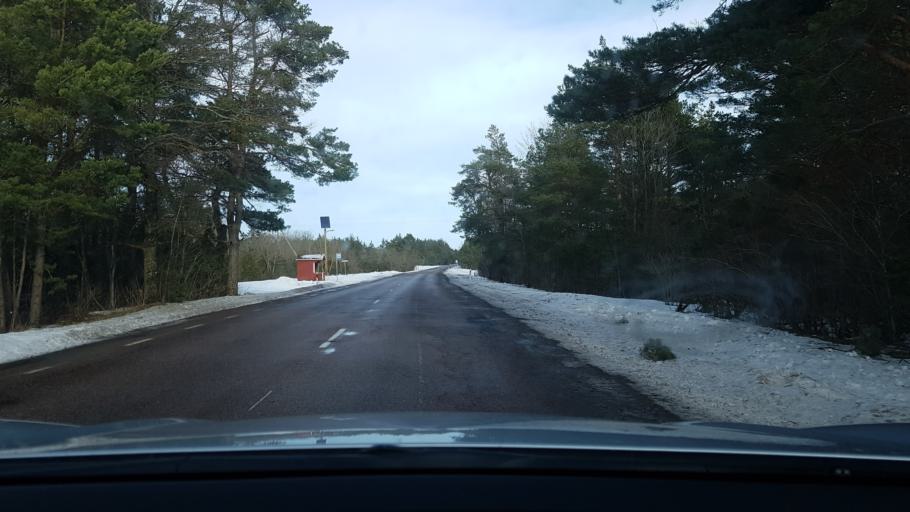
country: EE
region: Saare
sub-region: Kuressaare linn
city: Kuressaare
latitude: 58.3375
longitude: 22.5710
